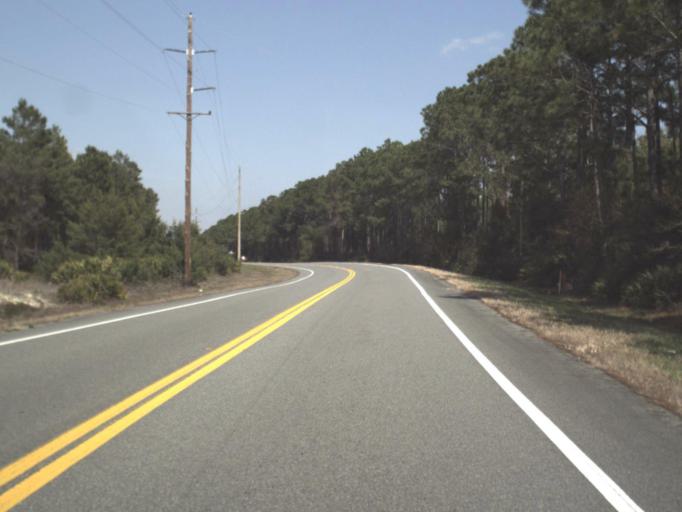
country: US
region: Florida
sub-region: Franklin County
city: Carrabelle
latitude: 29.9288
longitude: -84.5159
